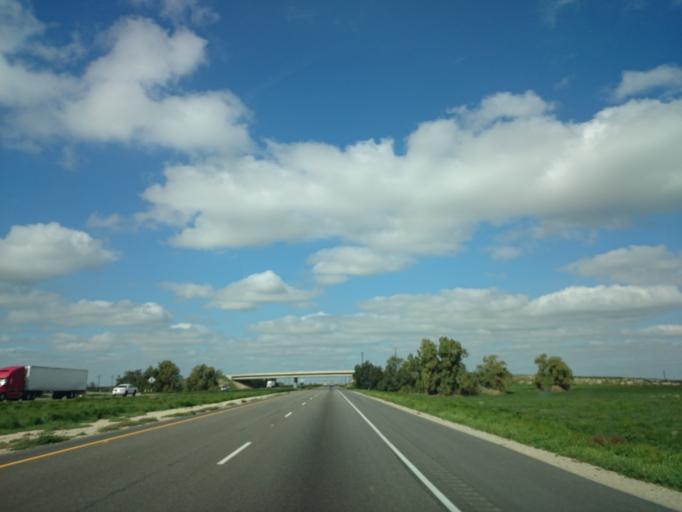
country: US
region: California
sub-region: Kern County
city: Greenfield
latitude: 35.2074
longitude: -119.1607
